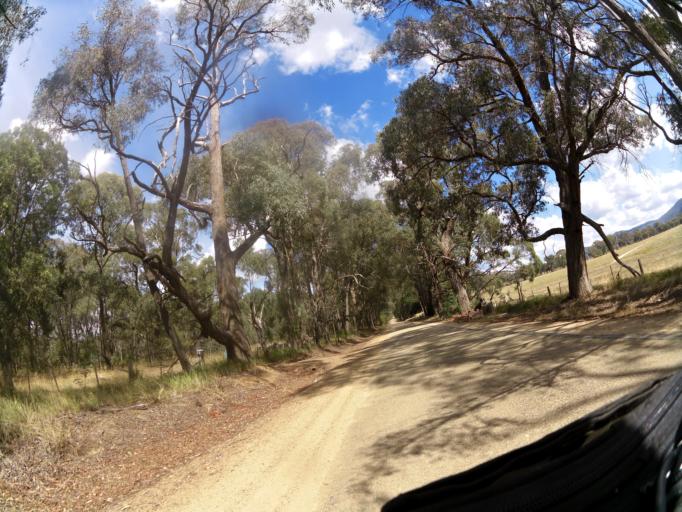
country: AU
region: Victoria
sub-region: Benalla
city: Benalla
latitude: -36.7744
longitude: 145.9743
